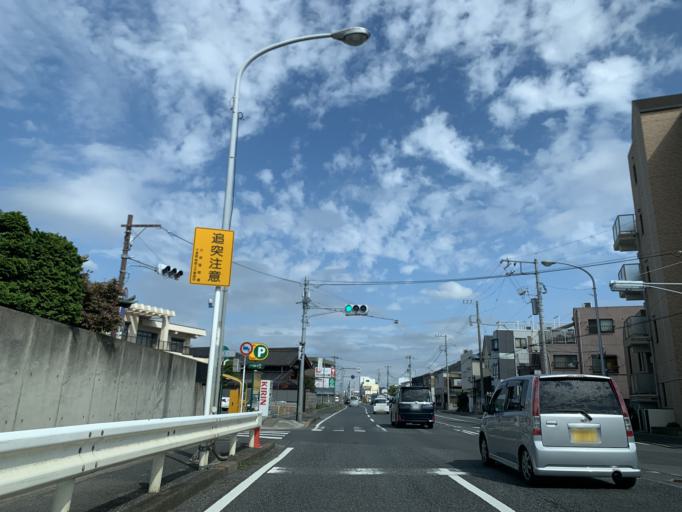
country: JP
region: Tokyo
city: Urayasu
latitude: 35.6937
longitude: 139.9231
